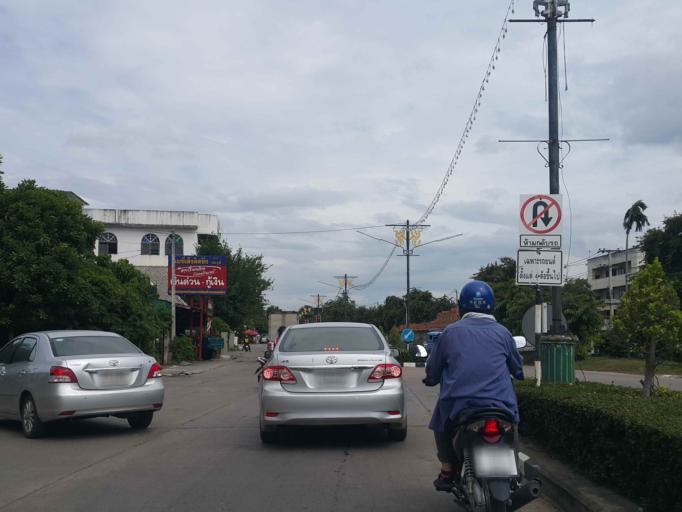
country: TH
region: Lamphun
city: Lamphun
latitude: 18.5733
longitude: 99.0051
